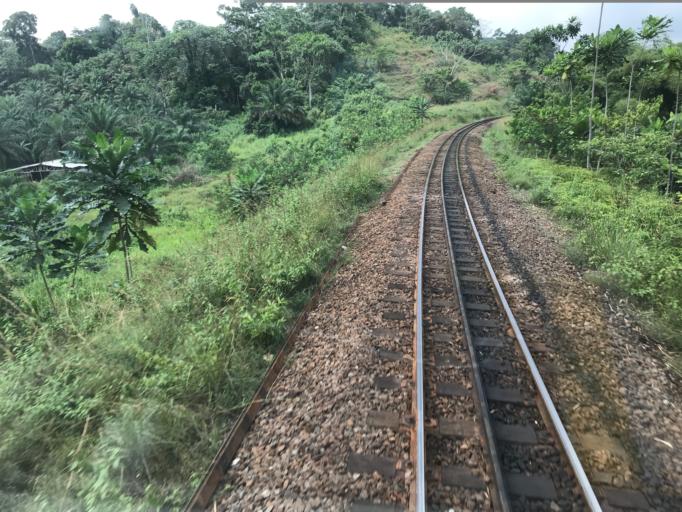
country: CM
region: Centre
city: Eseka
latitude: 3.5863
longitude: 10.8358
